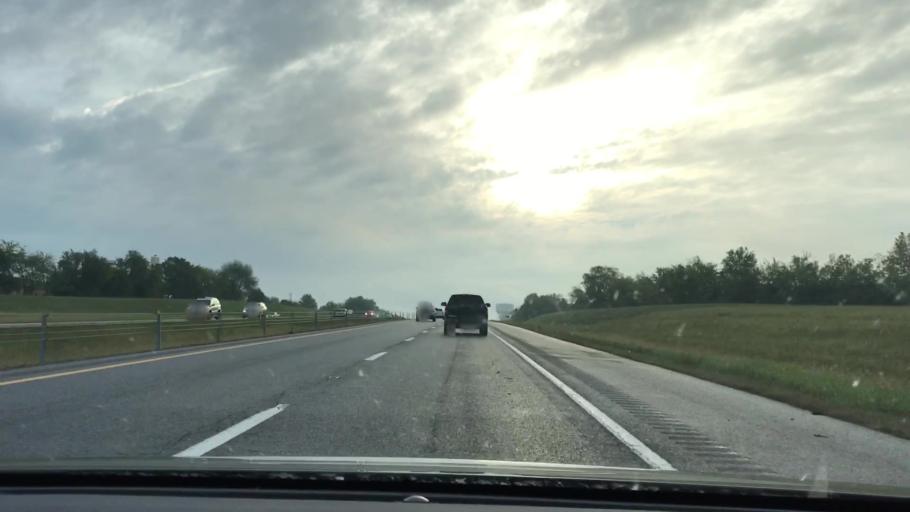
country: US
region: Tennessee
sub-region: Sumner County
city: Hendersonville
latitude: 36.3324
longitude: -86.5911
